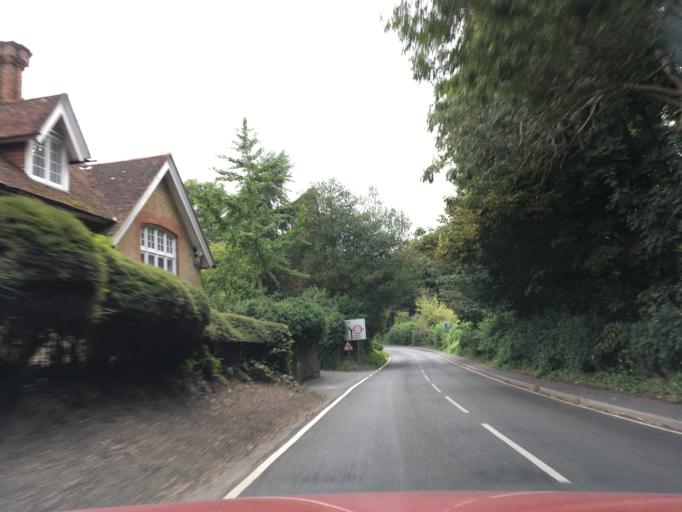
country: GB
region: England
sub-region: Kent
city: Wateringbury
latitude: 51.2514
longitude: 0.4555
